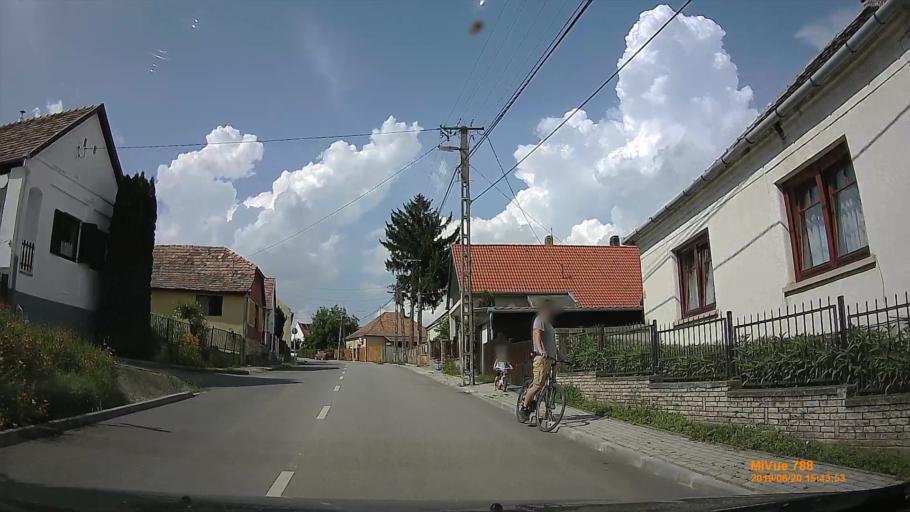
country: HU
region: Baranya
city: Kozarmisleny
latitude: 45.9835
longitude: 18.2608
